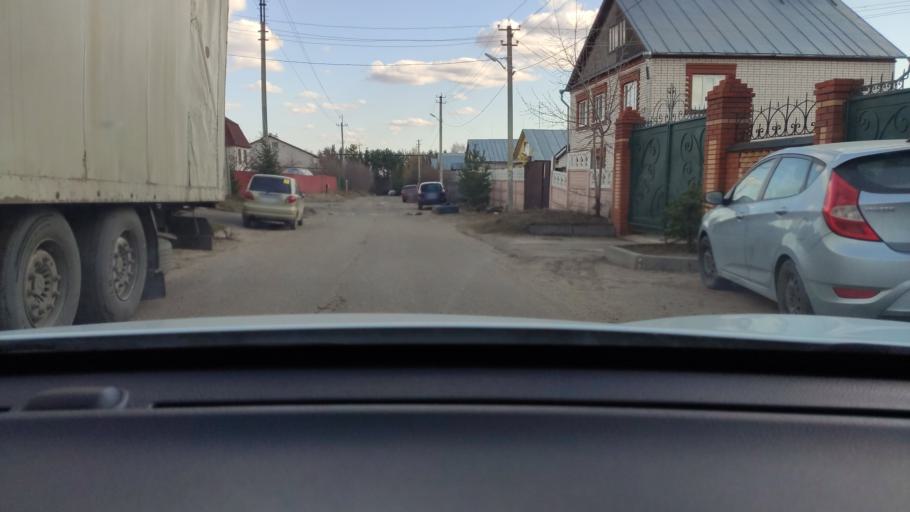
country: RU
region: Tatarstan
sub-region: Gorod Kazan'
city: Kazan
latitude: 55.8099
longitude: 49.2192
